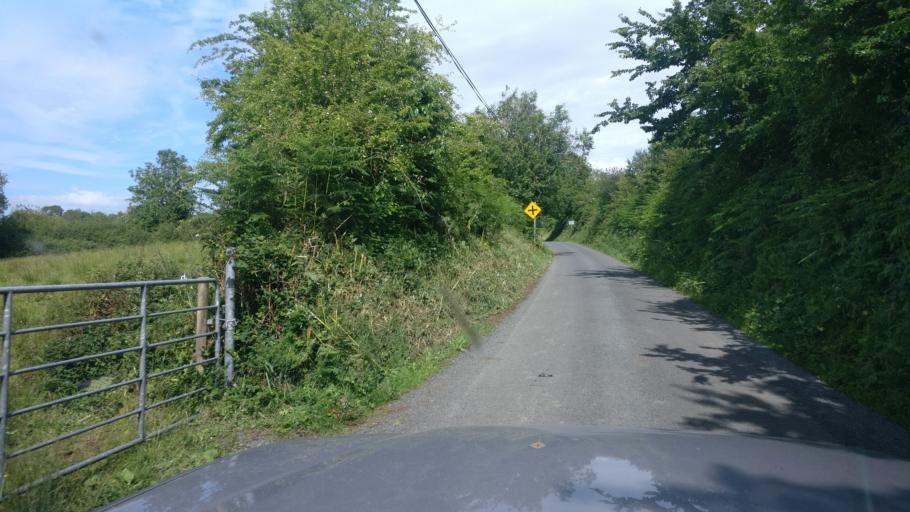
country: IE
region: Connaught
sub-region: County Galway
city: Gort
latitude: 53.0793
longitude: -8.7499
